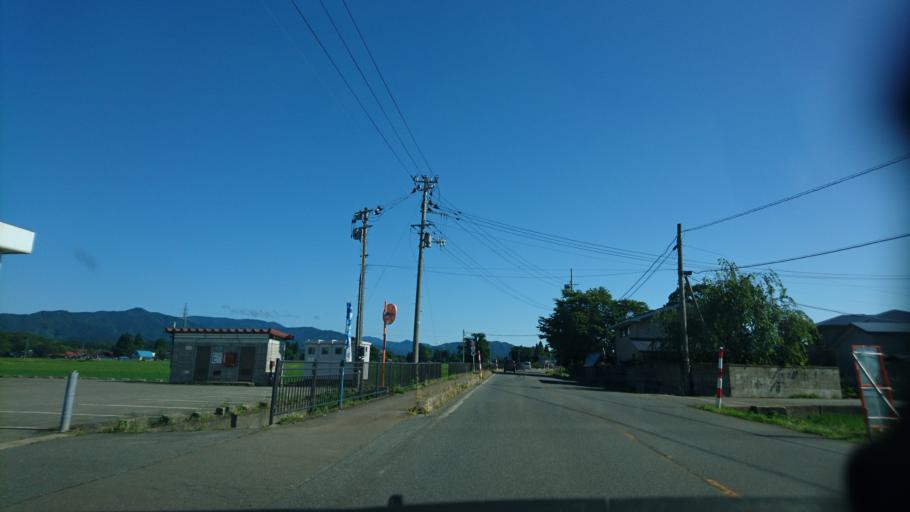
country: JP
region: Akita
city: Kakunodatemachi
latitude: 39.6154
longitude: 140.5712
